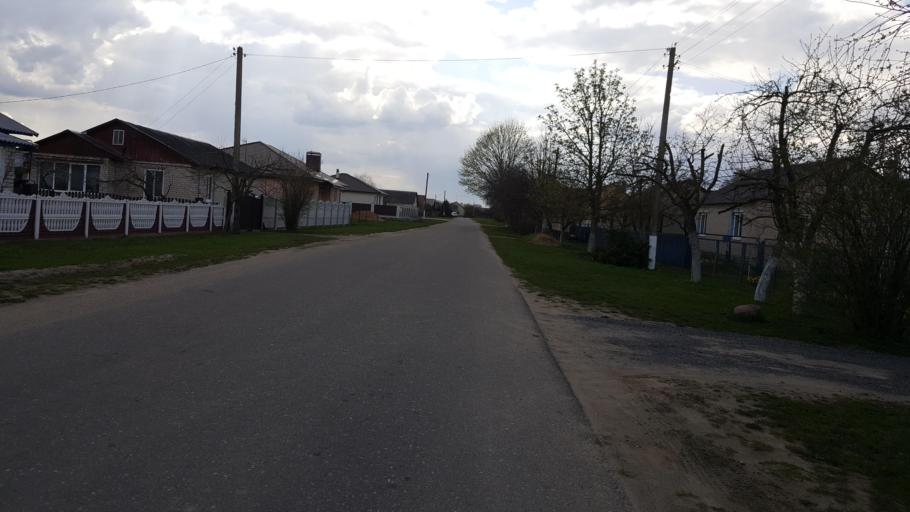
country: BY
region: Brest
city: Kamyanyets
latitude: 52.4106
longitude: 23.6166
